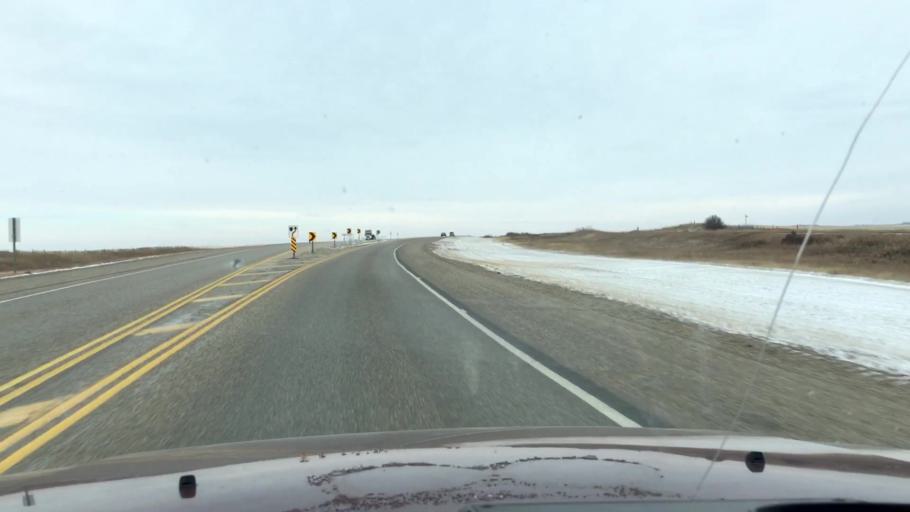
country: CA
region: Saskatchewan
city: Moose Jaw
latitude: 50.8439
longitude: -105.5531
